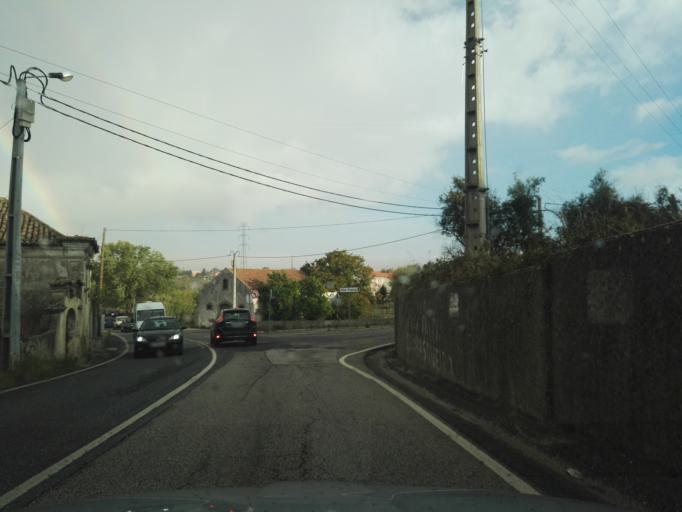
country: PT
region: Lisbon
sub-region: Arruda Dos Vinhos
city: Arruda dos Vinhos
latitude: 38.9707
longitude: -9.0650
